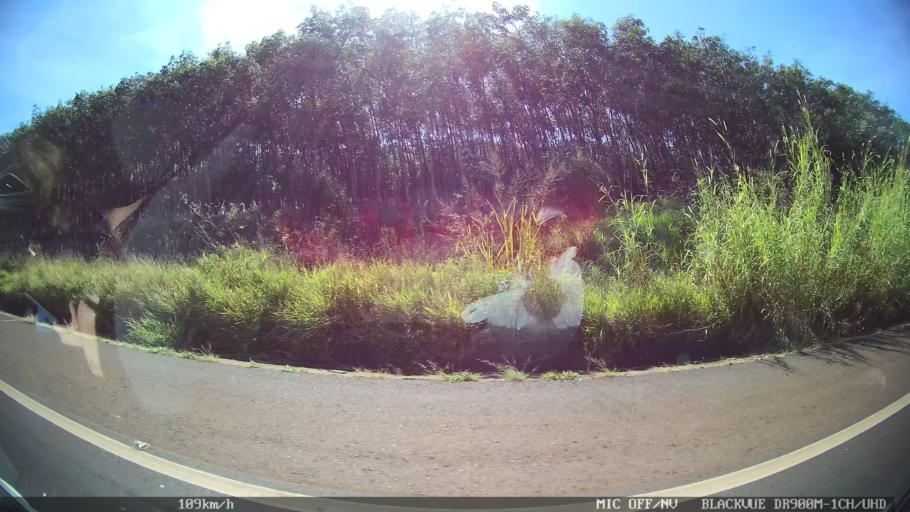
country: BR
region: Sao Paulo
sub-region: Franca
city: Franca
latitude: -20.5592
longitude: -47.5396
